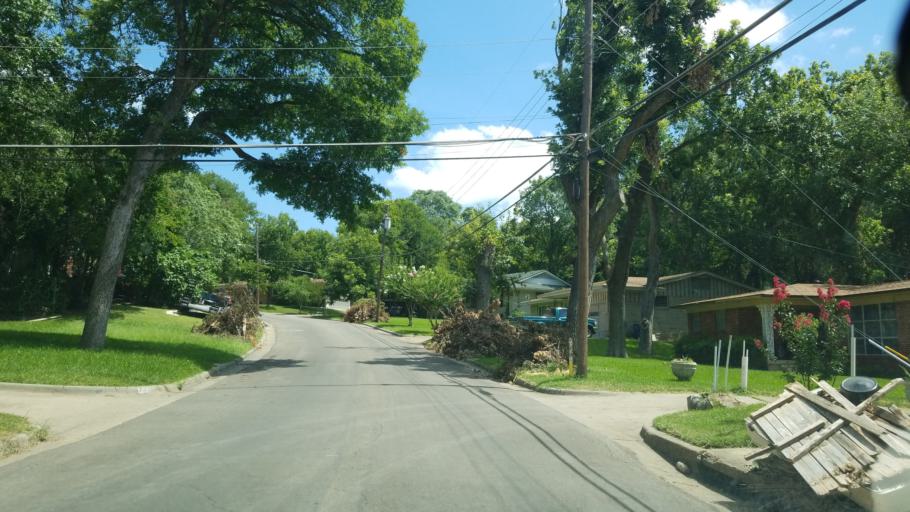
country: US
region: Texas
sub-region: Dallas County
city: Balch Springs
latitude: 32.7569
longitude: -96.6980
